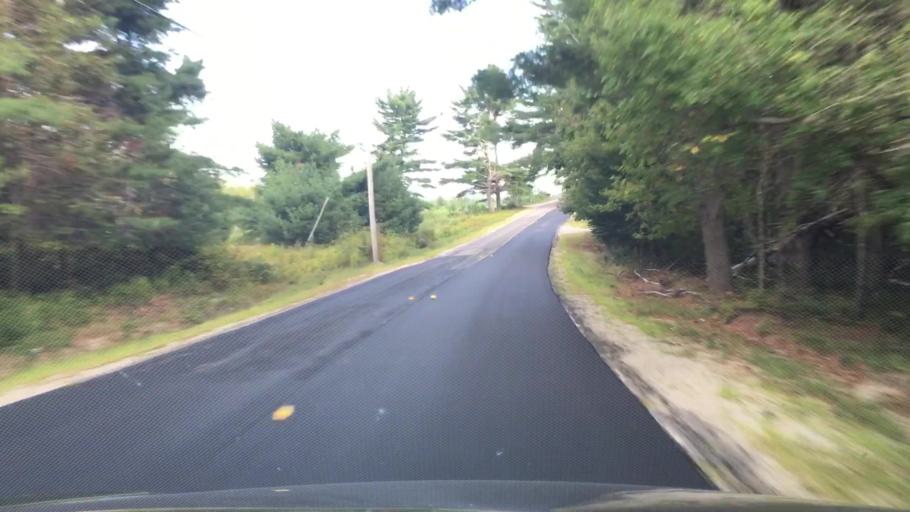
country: US
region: Maine
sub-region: Hancock County
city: Surry
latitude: 44.5164
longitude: -68.6049
